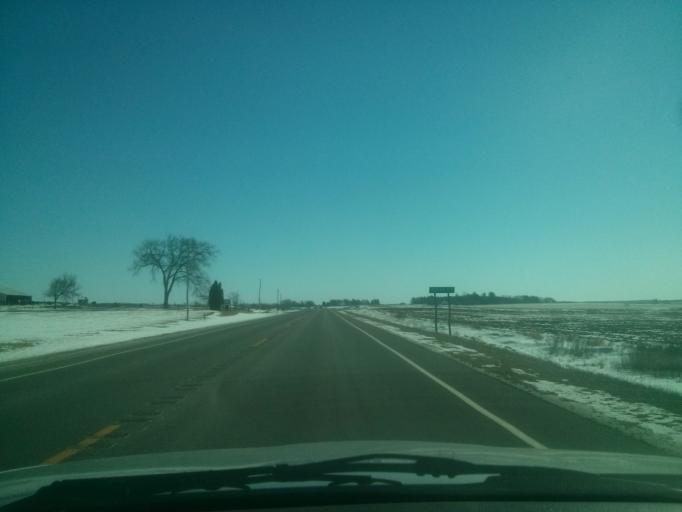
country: US
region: Wisconsin
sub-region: Polk County
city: Clear Lake
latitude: 45.1364
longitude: -92.3665
